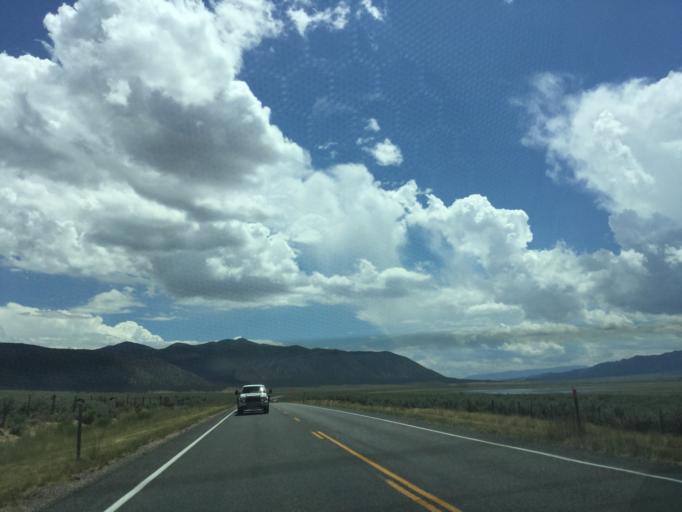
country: US
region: Utah
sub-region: Sanpete County
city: Centerfield
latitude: 39.1239
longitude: -112.0521
